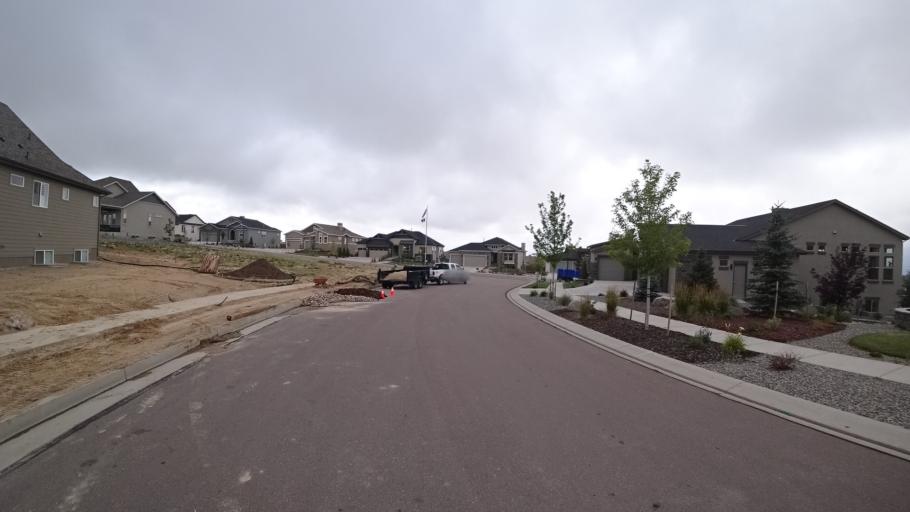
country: US
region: Colorado
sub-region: El Paso County
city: Gleneagle
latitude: 39.0098
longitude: -104.7859
